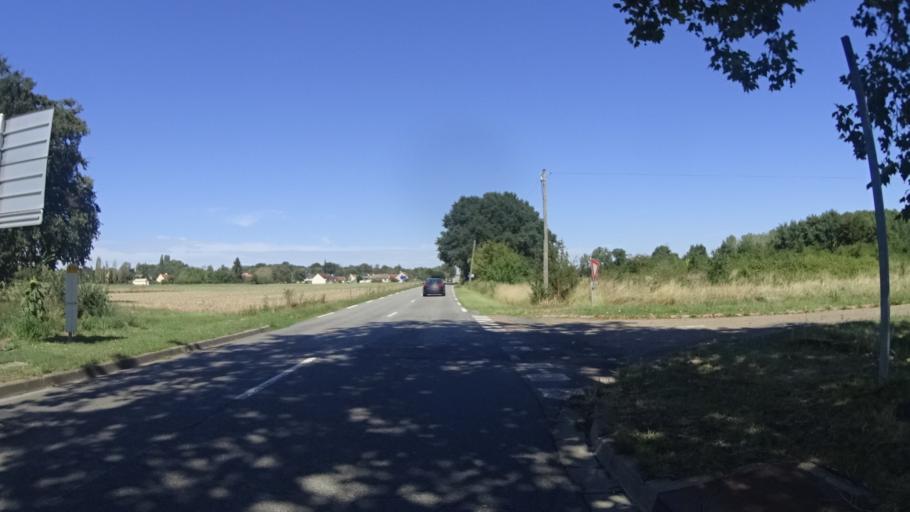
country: FR
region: Centre
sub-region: Departement du Cher
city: Belleville-sur-Loire
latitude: 47.5134
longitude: 2.8462
